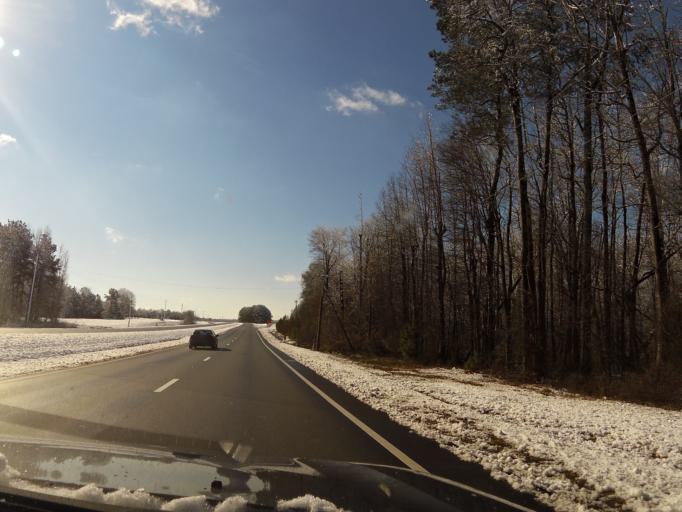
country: US
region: North Carolina
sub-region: Wilson County
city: Elm City
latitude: 35.8317
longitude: -77.8558
